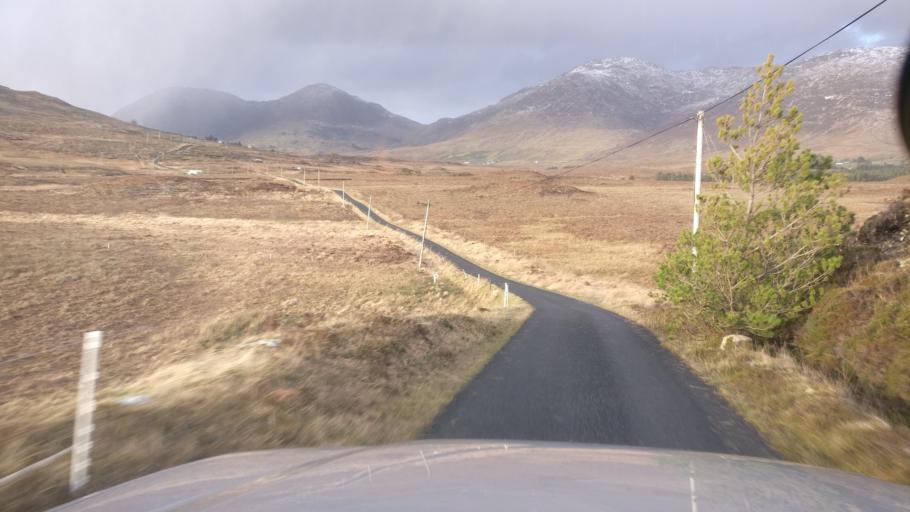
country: IE
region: Connaught
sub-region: County Galway
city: Clifden
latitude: 53.4746
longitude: -9.6923
